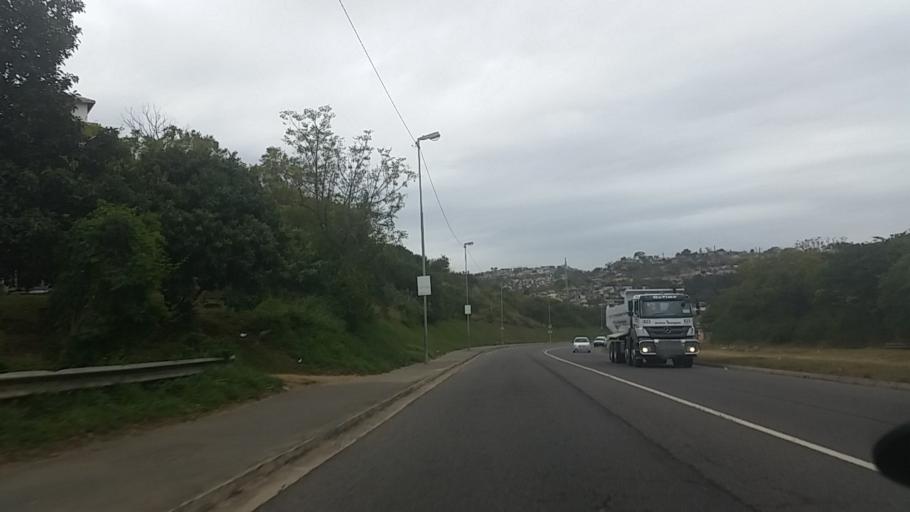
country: ZA
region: KwaZulu-Natal
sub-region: eThekwini Metropolitan Municipality
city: Berea
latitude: -29.8573
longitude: 30.9467
